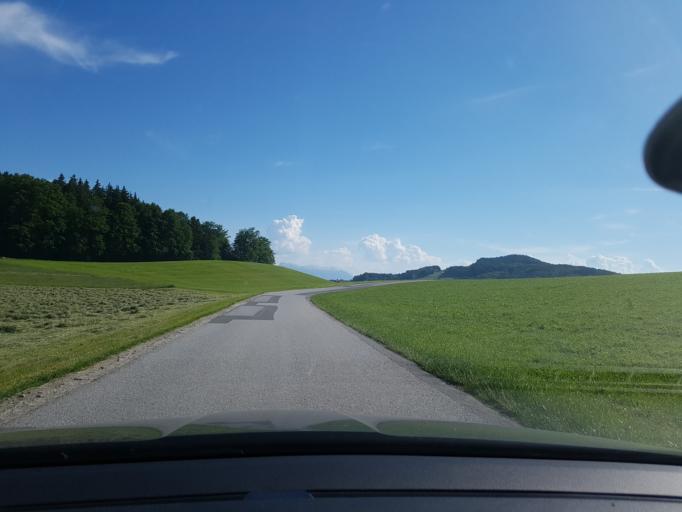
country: AT
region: Salzburg
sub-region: Politischer Bezirk Salzburg-Umgebung
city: Schleedorf
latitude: 47.9725
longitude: 13.1358
